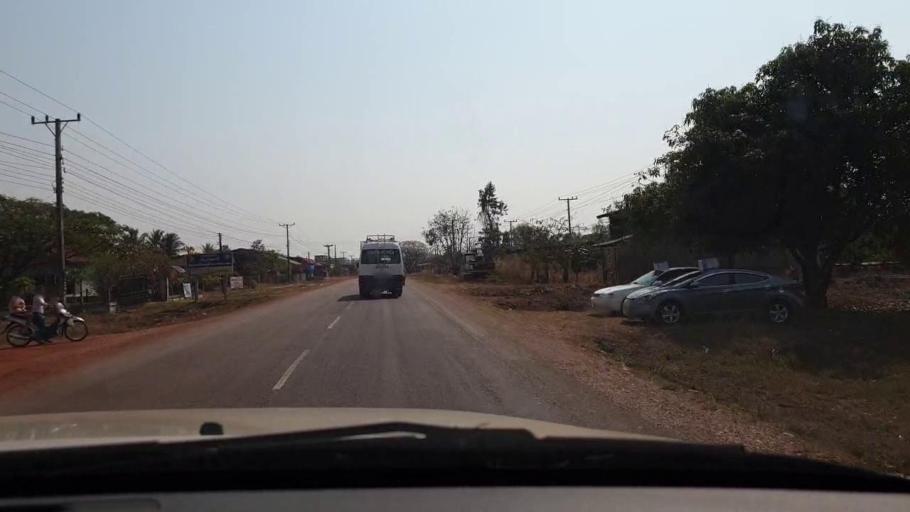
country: TH
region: Nong Khai
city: Nong Khai
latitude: 18.0546
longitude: 102.8351
